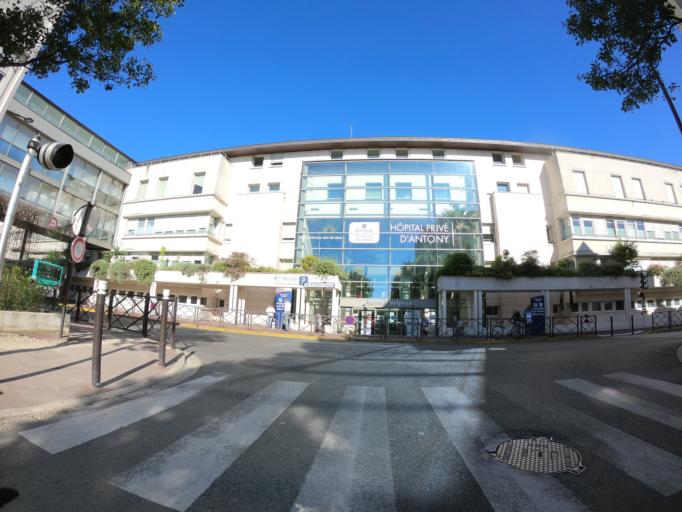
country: FR
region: Ile-de-France
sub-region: Departement des Hauts-de-Seine
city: Antony
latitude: 48.7566
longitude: 2.3026
